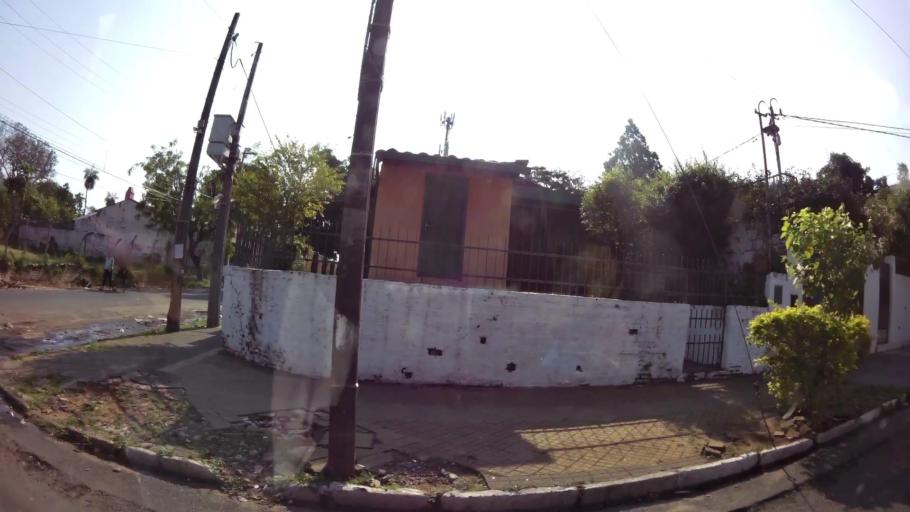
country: PY
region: Asuncion
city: Asuncion
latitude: -25.3062
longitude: -57.6288
